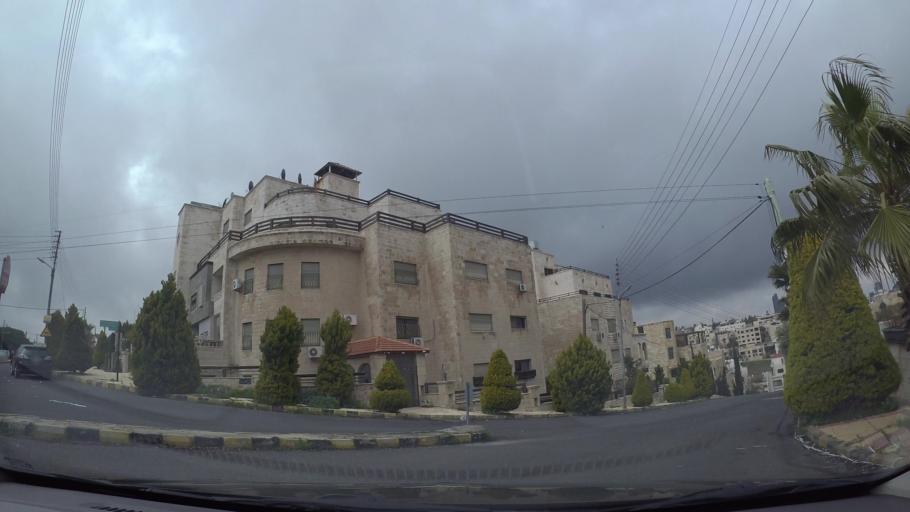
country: JO
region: Amman
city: Al Bunayyat ash Shamaliyah
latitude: 31.9403
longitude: 35.8942
